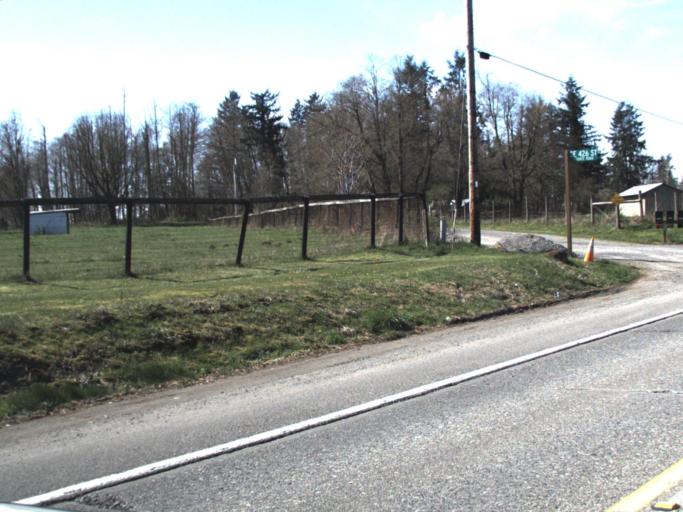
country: US
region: Washington
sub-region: Pierce County
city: Buckley
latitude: 47.2192
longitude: -122.0921
